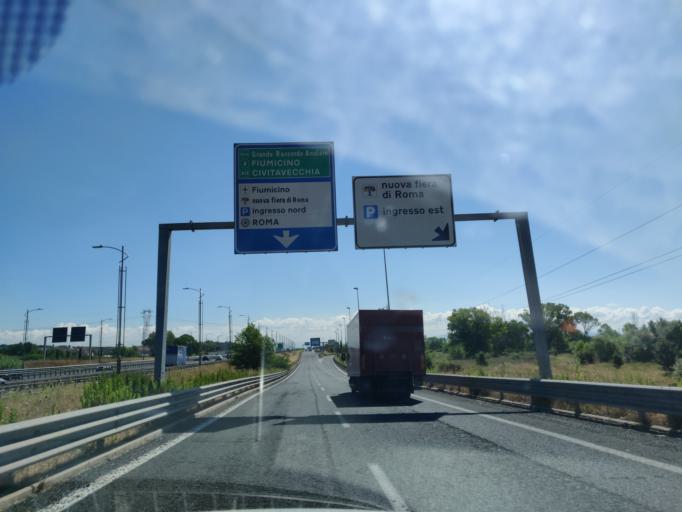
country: IT
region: Latium
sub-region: Citta metropolitana di Roma Capitale
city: Ponte Galeria-La Pisana
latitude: 41.8130
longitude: 12.3339
